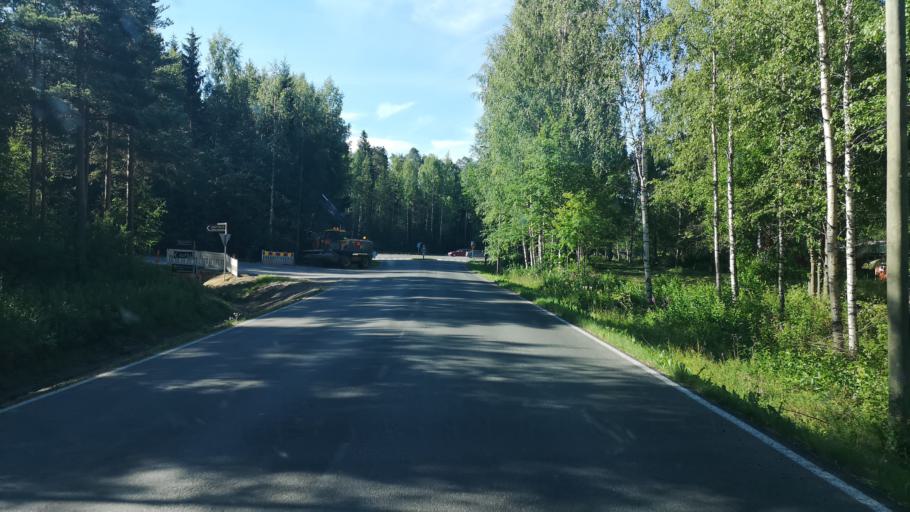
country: FI
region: Southern Ostrobothnia
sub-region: Seinaejoki
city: Lapua
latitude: 62.9706
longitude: 23.0540
